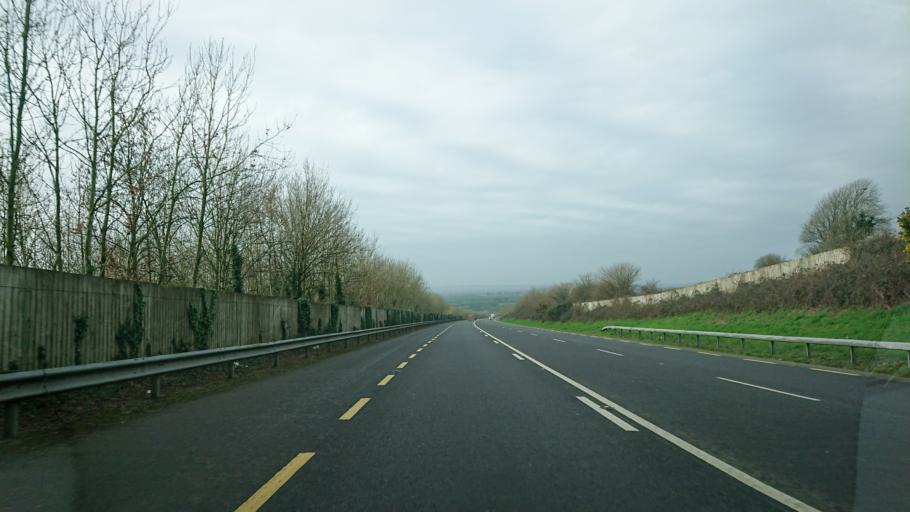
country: IE
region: Munster
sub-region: County Cork
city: Youghal
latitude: 51.9457
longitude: -7.8878
